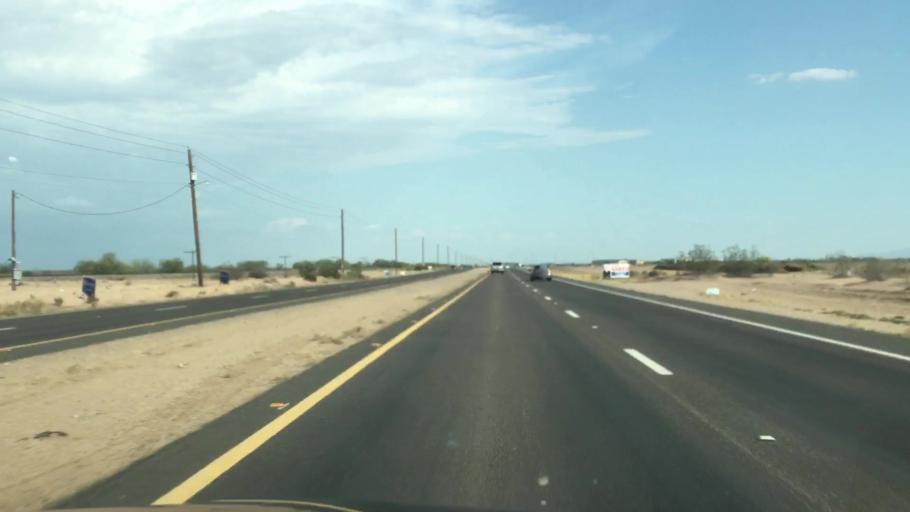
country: US
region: Arizona
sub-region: Pinal County
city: San Tan Valley
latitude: 33.1868
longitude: -111.5528
